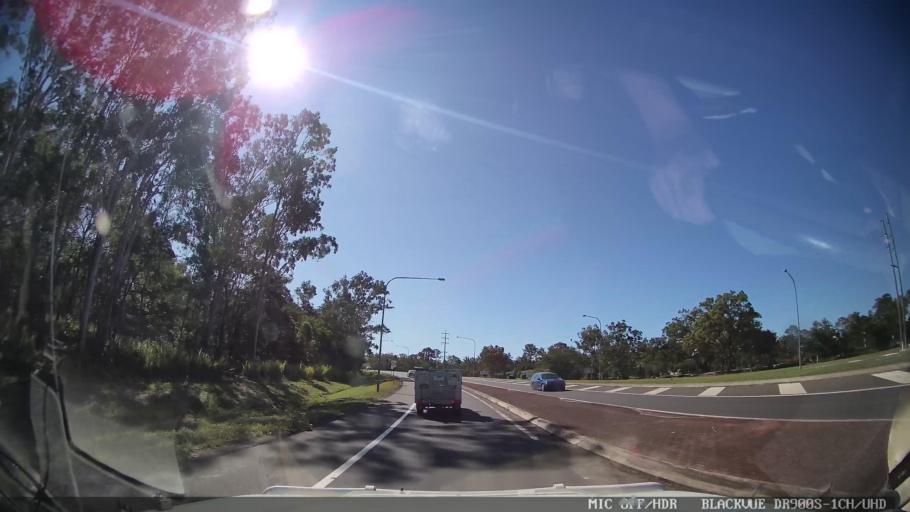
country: AU
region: Queensland
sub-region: Fraser Coast
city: Maryborough
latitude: -25.5137
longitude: 152.6709
